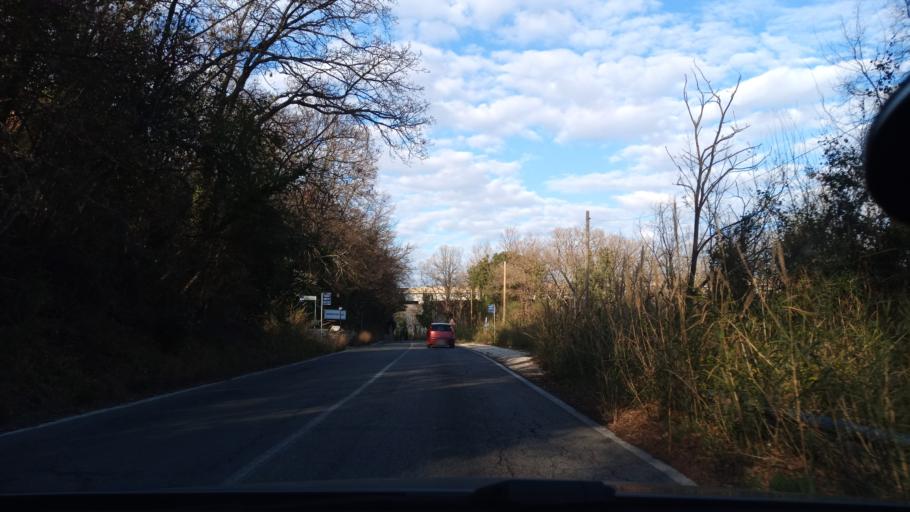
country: IT
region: Latium
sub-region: Citta metropolitana di Roma Capitale
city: Nazzano
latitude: 42.2119
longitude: 12.5993
